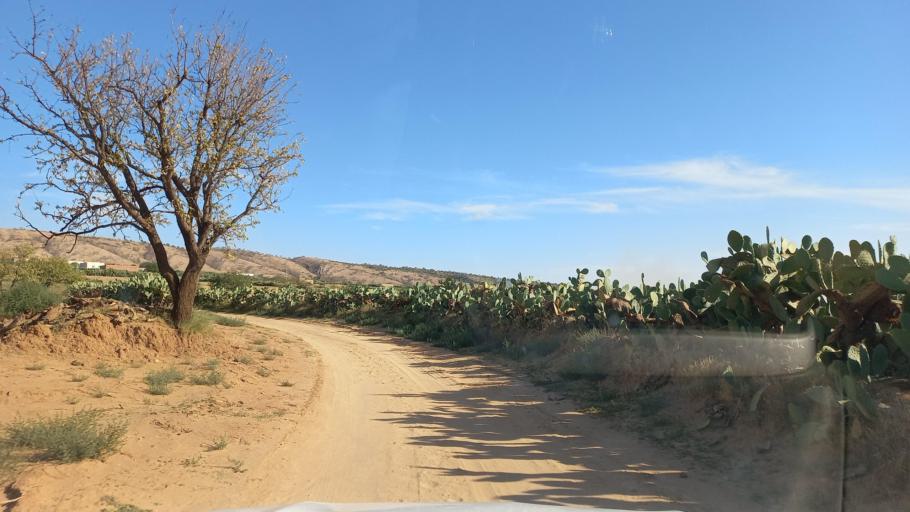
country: TN
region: Al Qasrayn
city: Sbiba
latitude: 35.3308
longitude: 9.1248
